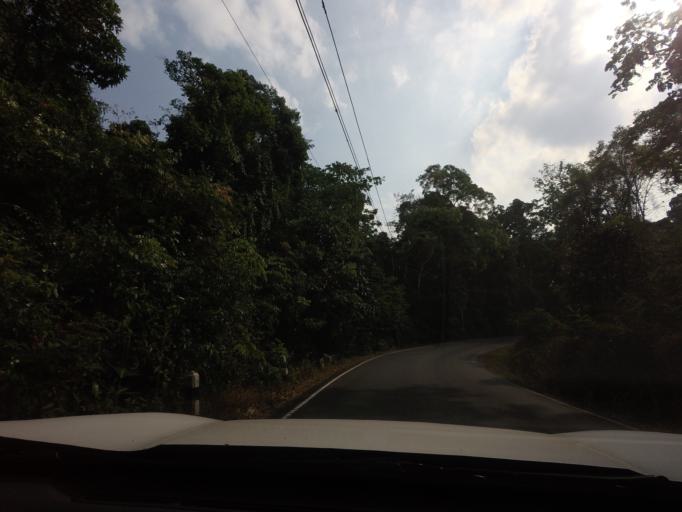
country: TH
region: Nakhon Ratchasima
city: Pak Chong
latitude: 14.4546
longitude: 101.3760
